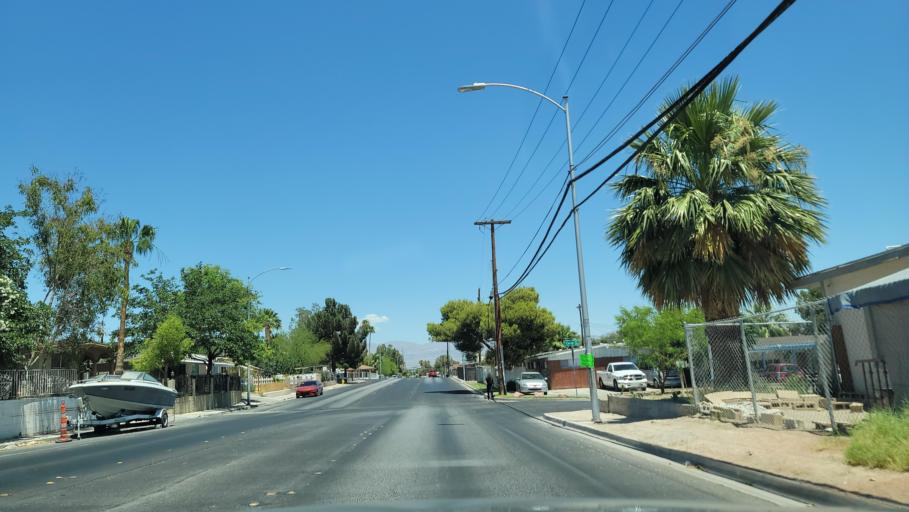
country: US
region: Nevada
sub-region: Clark County
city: Las Vegas
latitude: 36.1698
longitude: -115.1251
